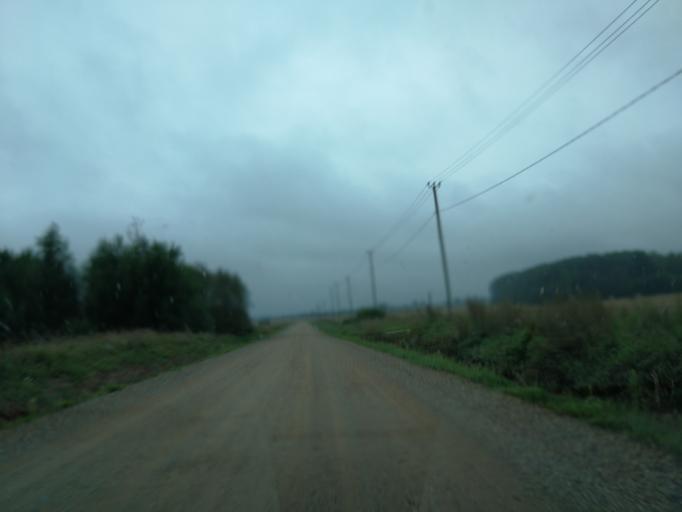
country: LV
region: Vilanu
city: Vilani
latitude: 56.3759
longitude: 27.0476
